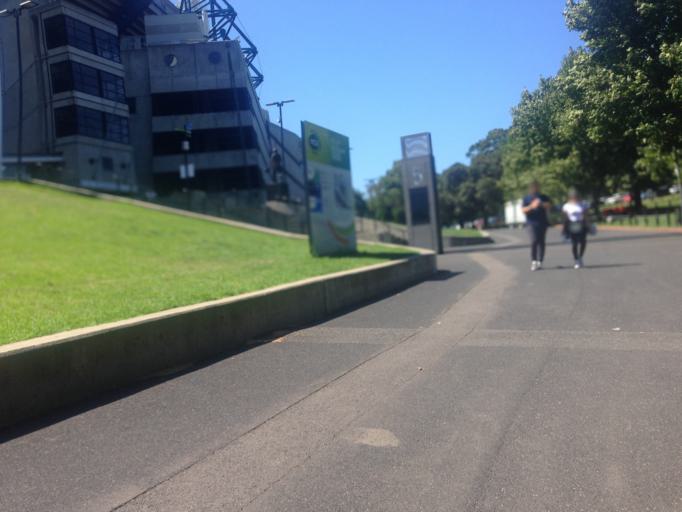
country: AU
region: Victoria
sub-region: Melbourne
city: East Melbourne
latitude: -37.8210
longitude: 144.9849
